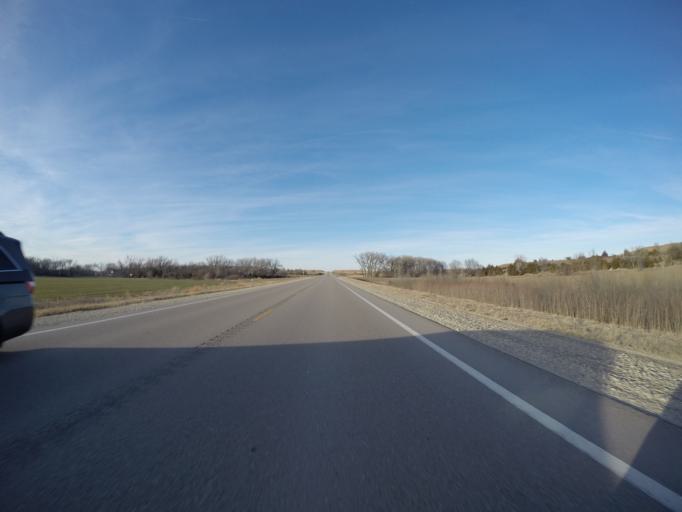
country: US
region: Kansas
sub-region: Marion County
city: Marion
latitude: 38.2739
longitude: -96.9616
